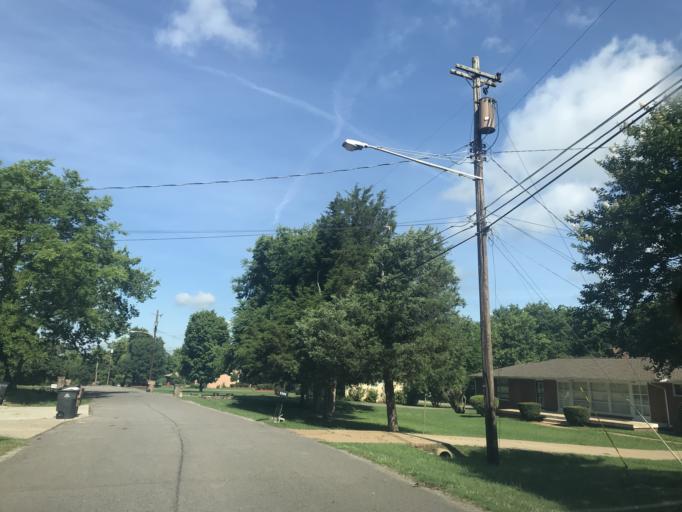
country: US
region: Tennessee
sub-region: Davidson County
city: Nashville
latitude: 36.2043
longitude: -86.8466
